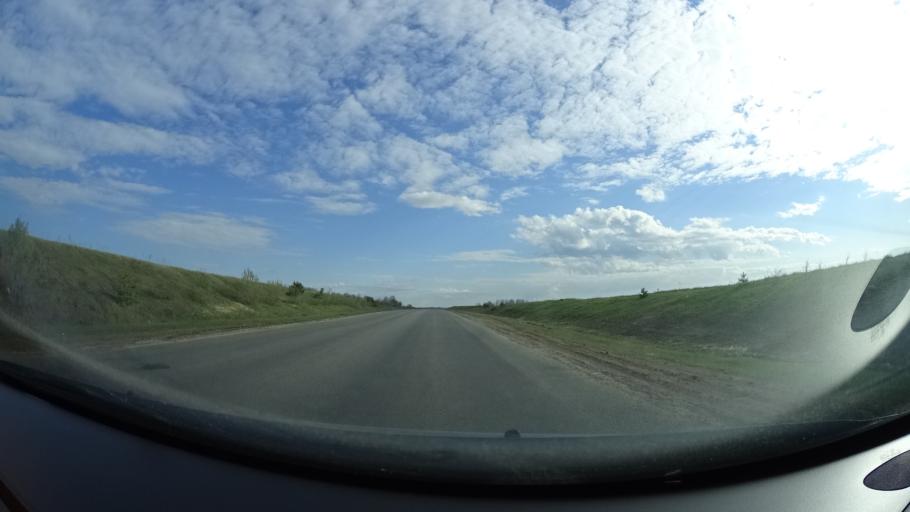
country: RU
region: Bashkortostan
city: Blagoveshchensk
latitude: 55.0896
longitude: 55.8111
